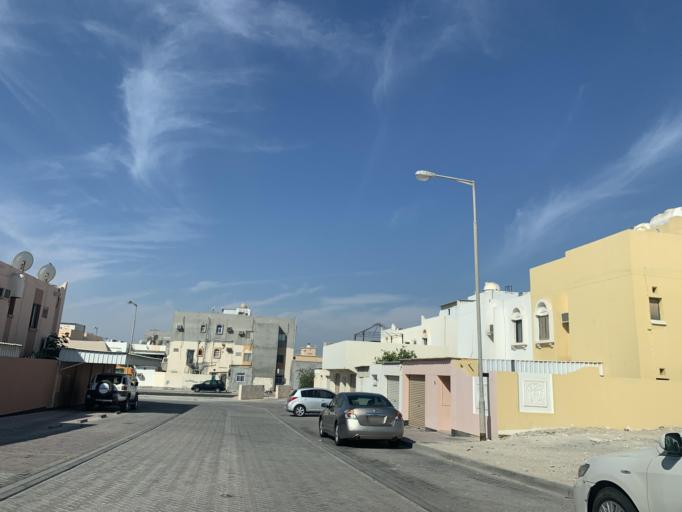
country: BH
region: Central Governorate
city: Madinat Hamad
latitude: 26.1253
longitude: 50.4961
